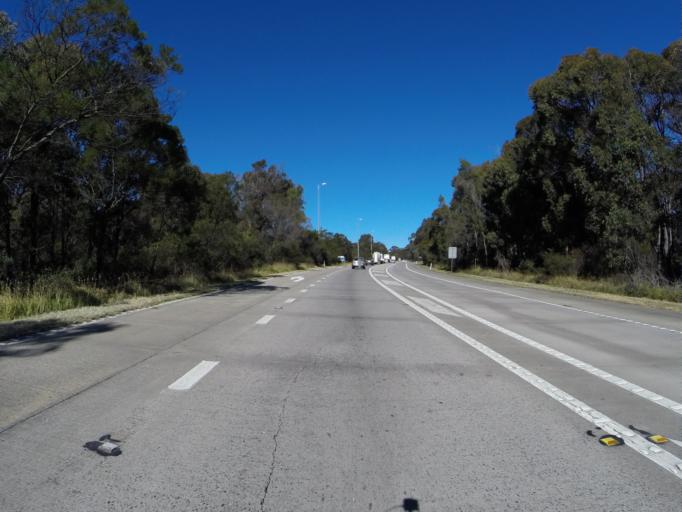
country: AU
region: New South Wales
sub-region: Wollondilly
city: Douglas Park
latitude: -34.2654
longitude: 150.7149
